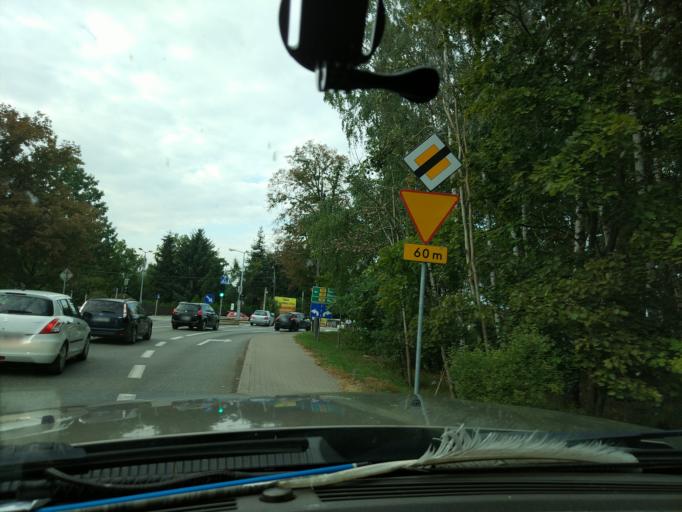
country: PL
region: Masovian Voivodeship
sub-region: Powiat pruszkowski
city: Otrebusy
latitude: 52.1306
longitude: 20.7565
